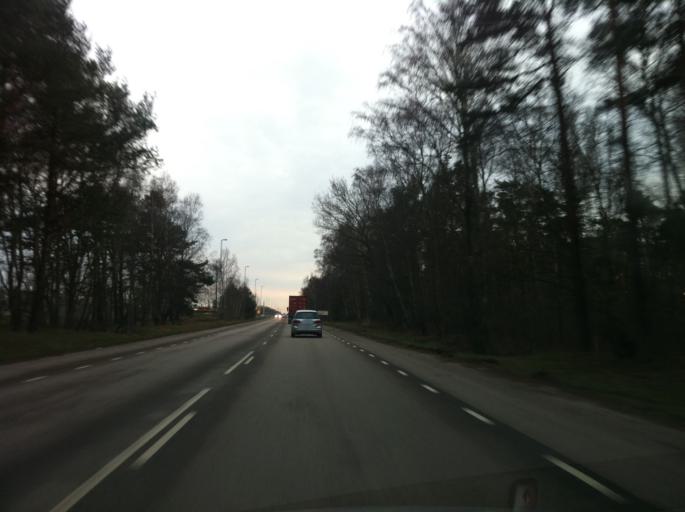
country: SE
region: Skane
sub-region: Hoganas Kommun
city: Hoganas
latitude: 56.1857
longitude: 12.5620
